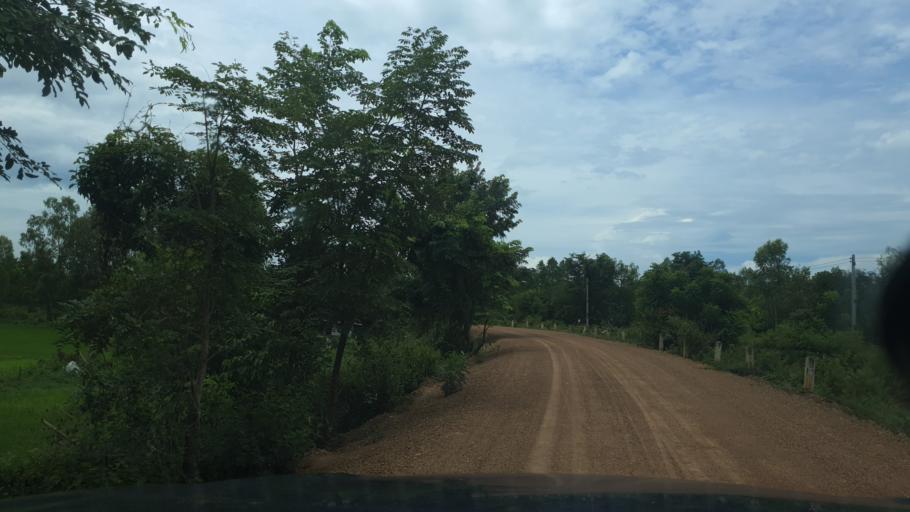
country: TH
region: Lampang
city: Hang Chat
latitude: 18.2824
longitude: 99.3722
